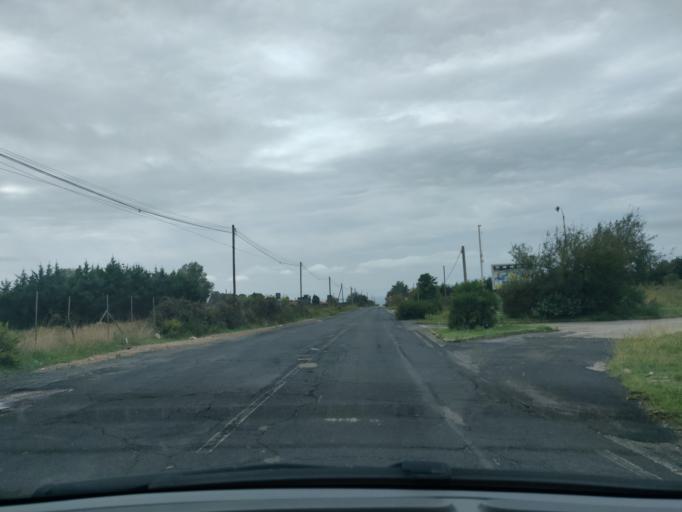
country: IT
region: Latium
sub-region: Citta metropolitana di Roma Capitale
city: Civitavecchia
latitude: 42.1073
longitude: 11.8314
